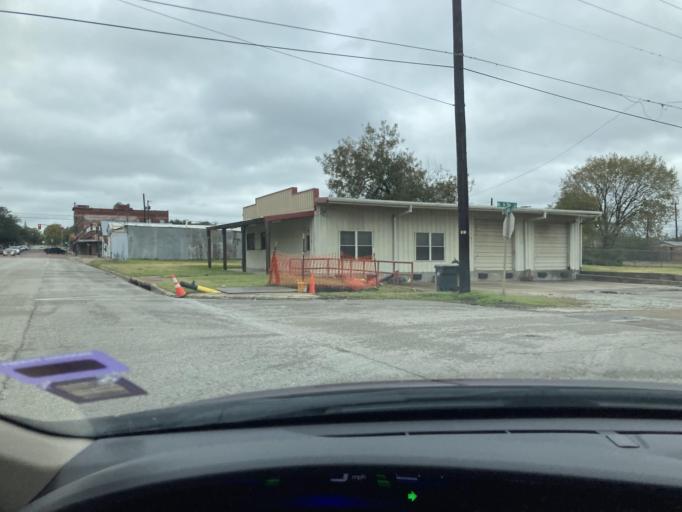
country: US
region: Texas
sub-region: Navarro County
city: Corsicana
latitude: 32.0972
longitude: -96.4636
